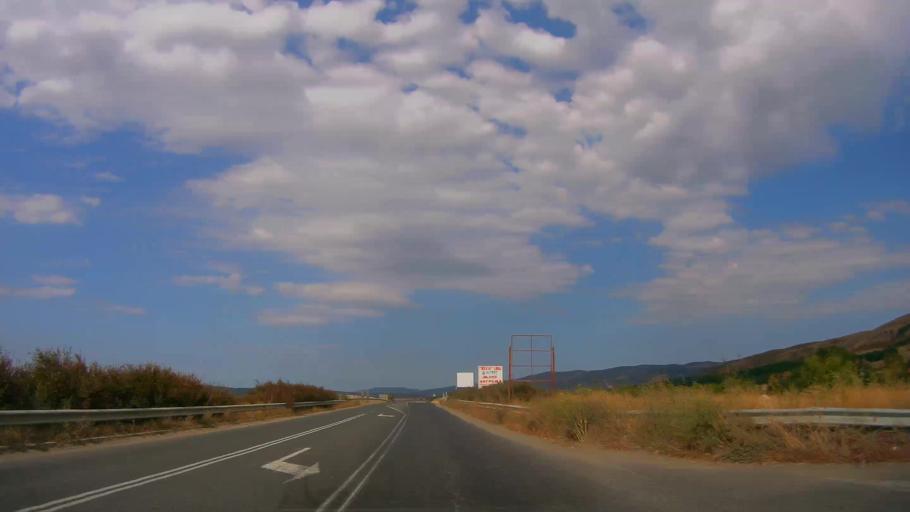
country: BG
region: Burgas
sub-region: Obshtina Aytos
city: Aytos
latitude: 42.7037
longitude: 27.2429
